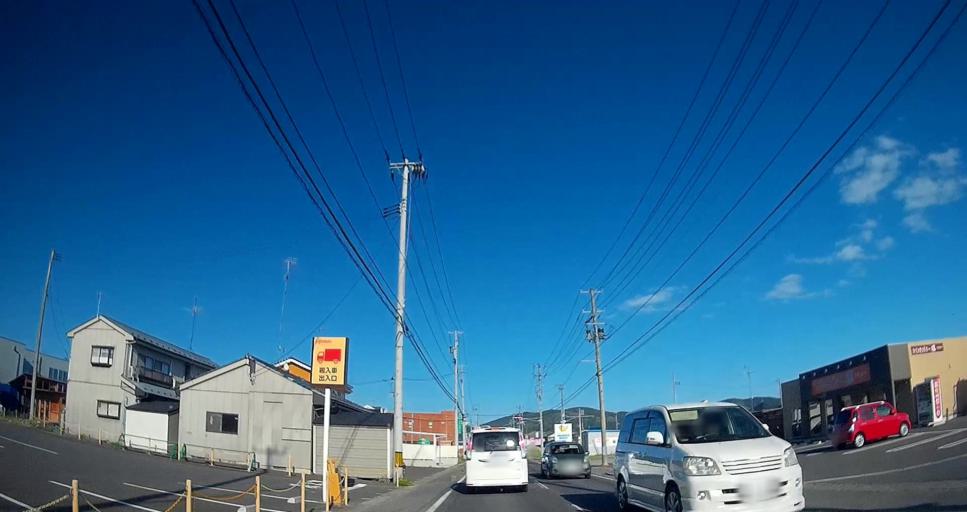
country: JP
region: Miyagi
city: Ishinomaki
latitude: 38.4183
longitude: 141.3402
